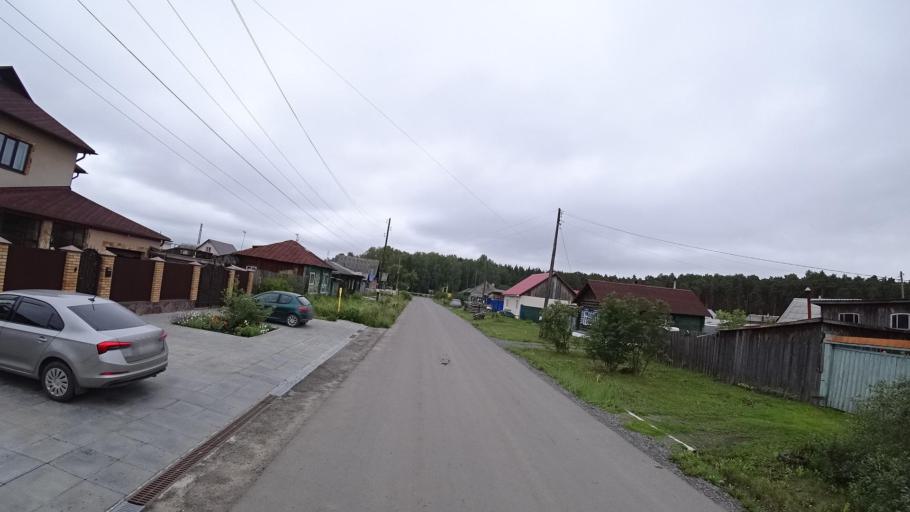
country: RU
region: Sverdlovsk
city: Kamyshlov
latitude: 56.8439
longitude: 62.7524
